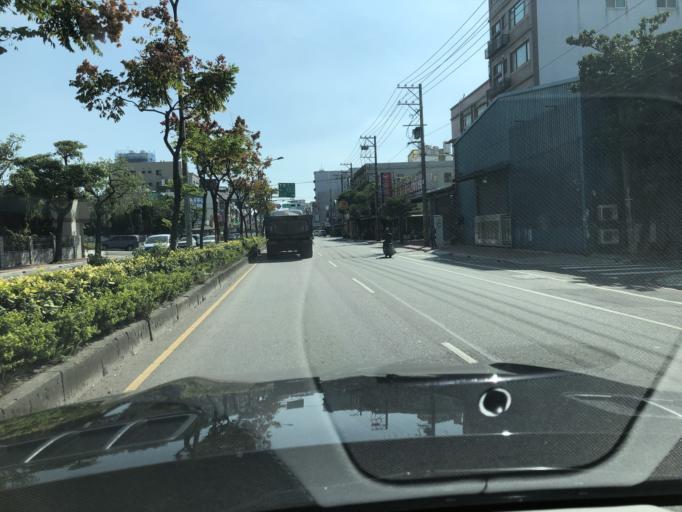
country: TW
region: Taiwan
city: Taoyuan City
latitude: 25.0740
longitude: 121.2852
